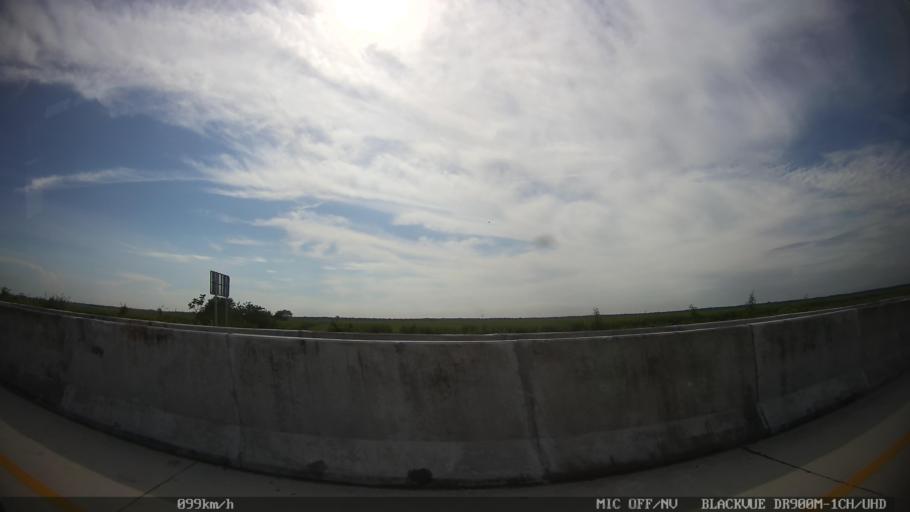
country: ID
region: North Sumatra
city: Binjai
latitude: 3.6724
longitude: 98.5349
